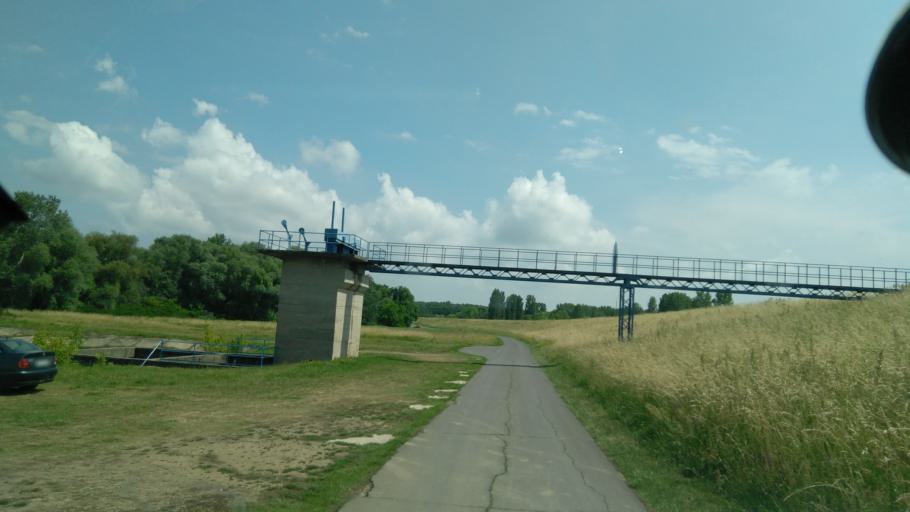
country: HU
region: Bekes
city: Bekes
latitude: 46.7632
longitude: 21.1508
